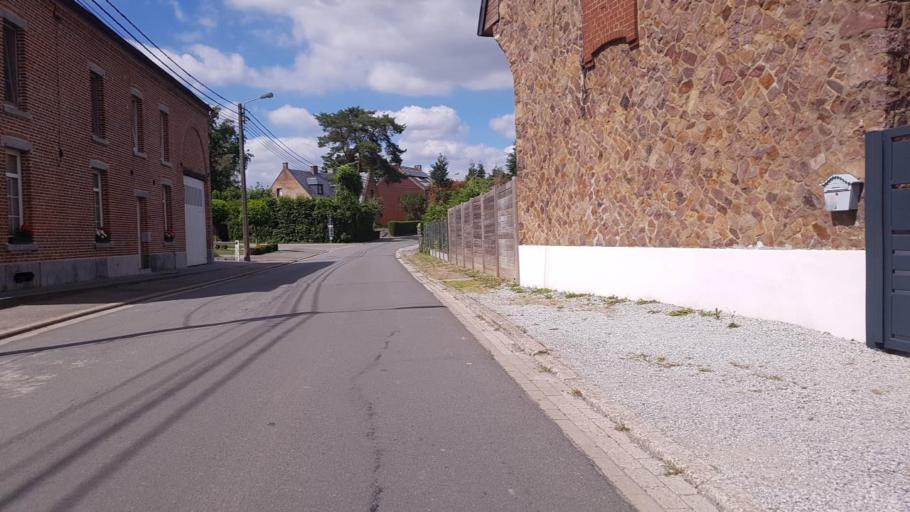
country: BE
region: Wallonia
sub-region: Province du Hainaut
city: Charleroi
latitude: 50.3408
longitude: 4.3969
